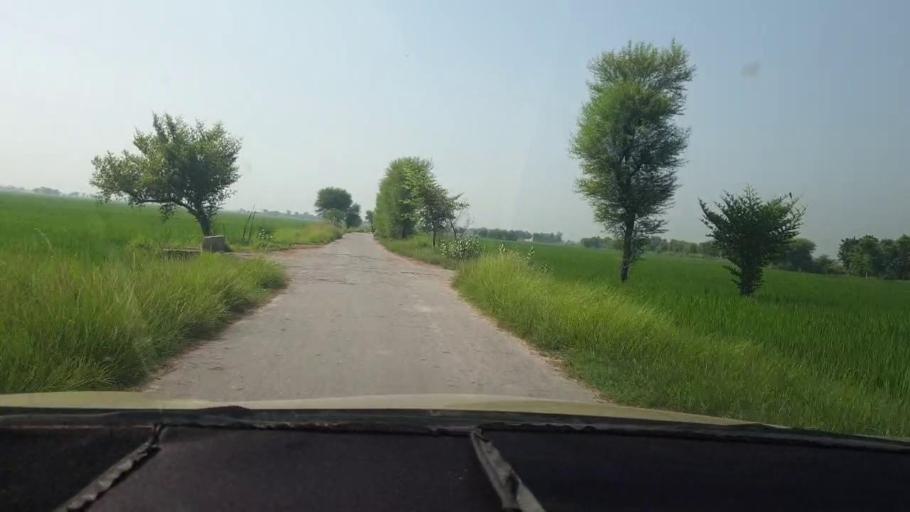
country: PK
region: Sindh
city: Kambar
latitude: 27.5802
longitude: 68.0553
